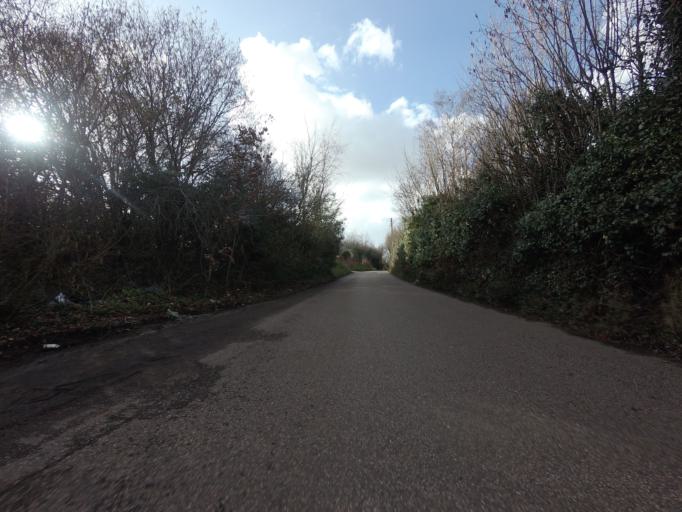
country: GB
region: England
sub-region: Kent
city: Swanley
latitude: 51.4054
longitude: 0.1804
